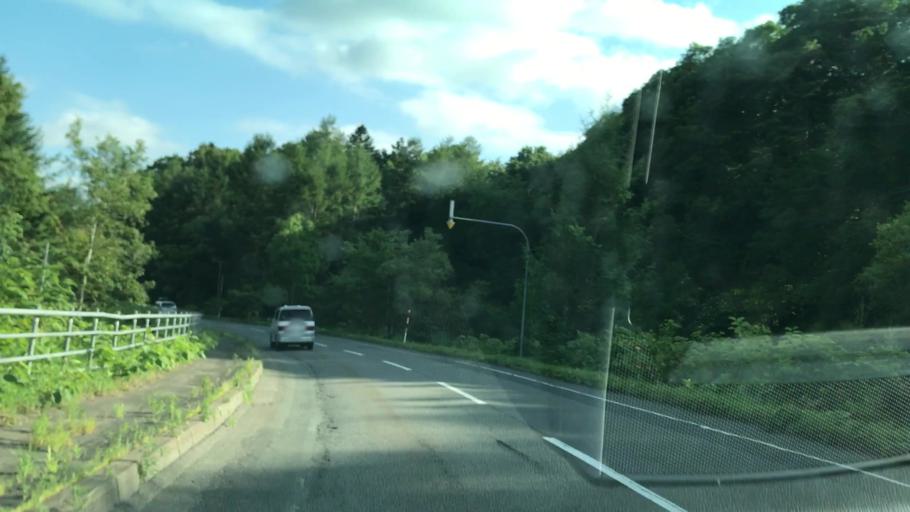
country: JP
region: Hokkaido
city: Shimo-furano
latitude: 42.8786
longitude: 142.1685
